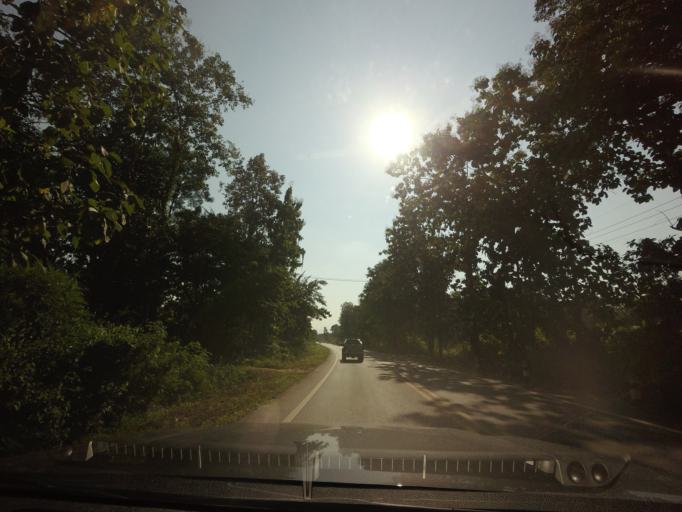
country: TH
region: Nan
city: Nan
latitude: 18.8135
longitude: 100.8057
